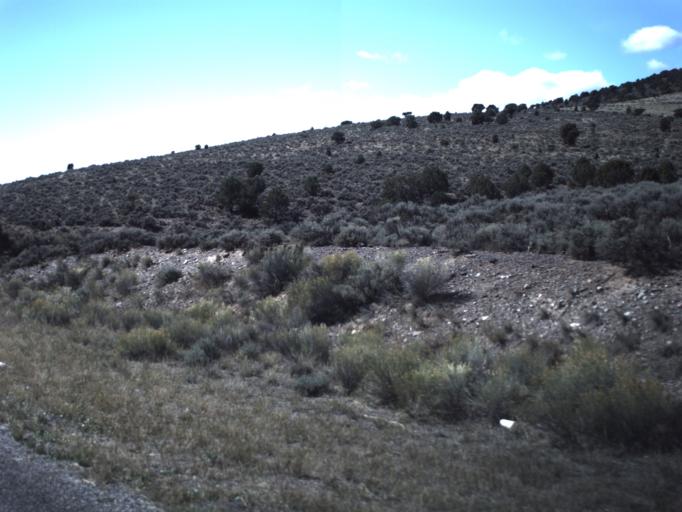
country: US
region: Utah
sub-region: Sevier County
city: Monroe
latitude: 38.5458
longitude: -111.8703
